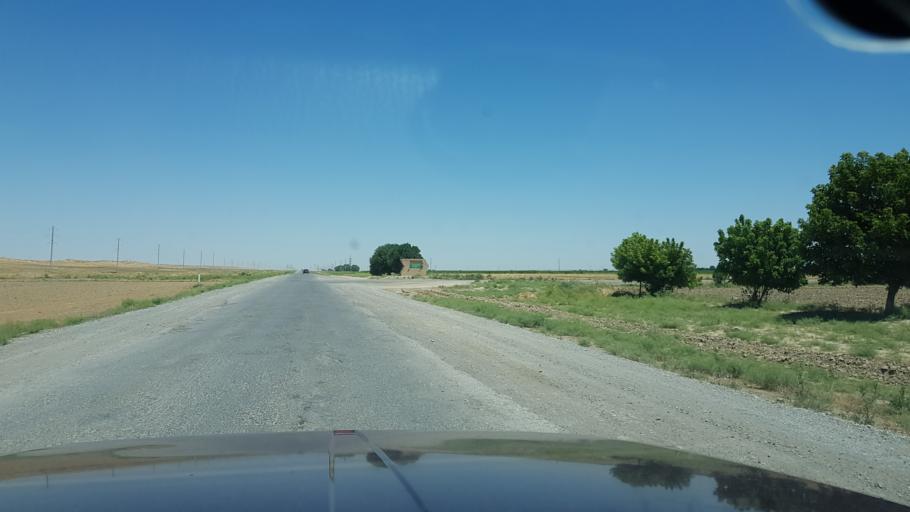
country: TM
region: Ahal
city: Annau
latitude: 37.8604
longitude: 58.7093
